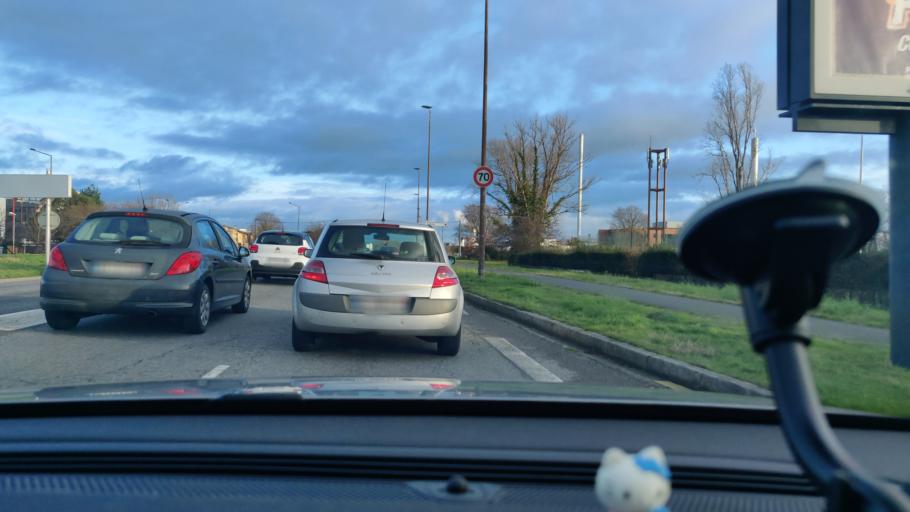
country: FR
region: Midi-Pyrenees
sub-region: Departement de la Haute-Garonne
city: Portet-sur-Garonne
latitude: 43.5644
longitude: 1.3849
